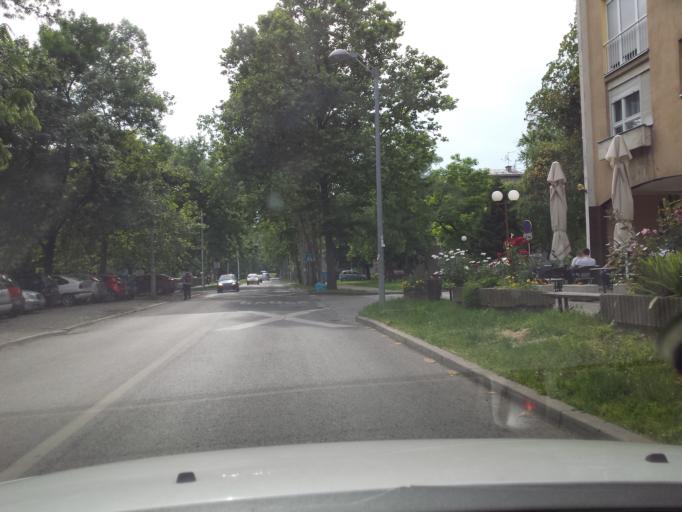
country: HR
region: Grad Zagreb
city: Jankomir
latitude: 45.8006
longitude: 15.9291
